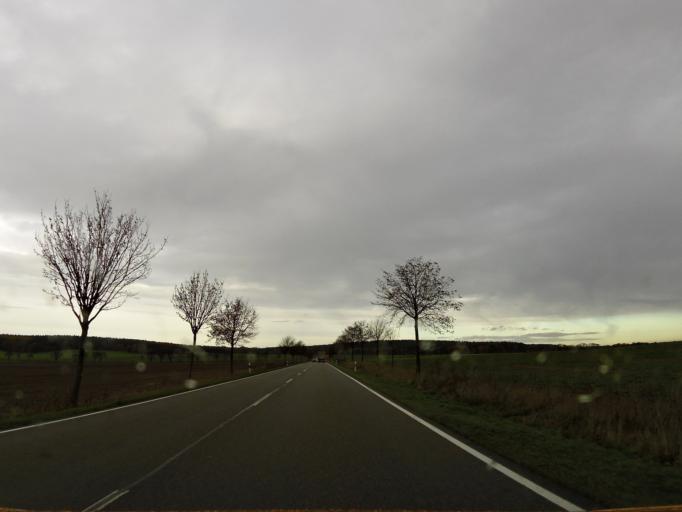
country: DE
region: Saxony-Anhalt
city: Kalbe
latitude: 52.6091
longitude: 11.3226
